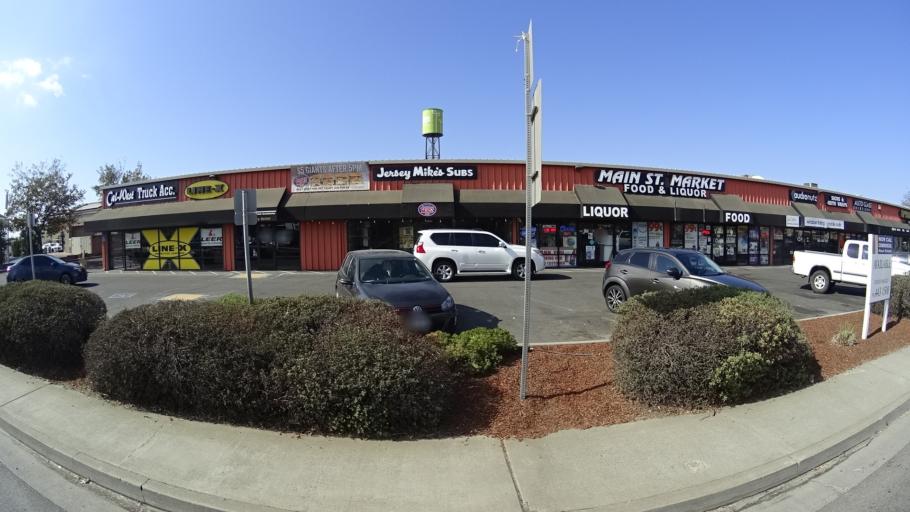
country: US
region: California
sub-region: Yolo County
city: Woodland
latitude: 38.6765
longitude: -121.7287
